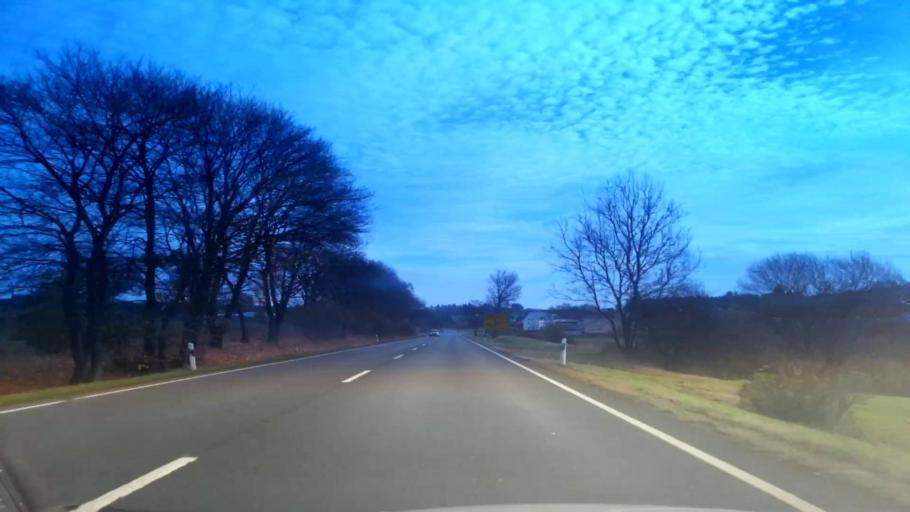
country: DE
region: Bavaria
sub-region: Upper Palatinate
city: Pechbrunn
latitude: 49.9746
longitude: 12.1597
